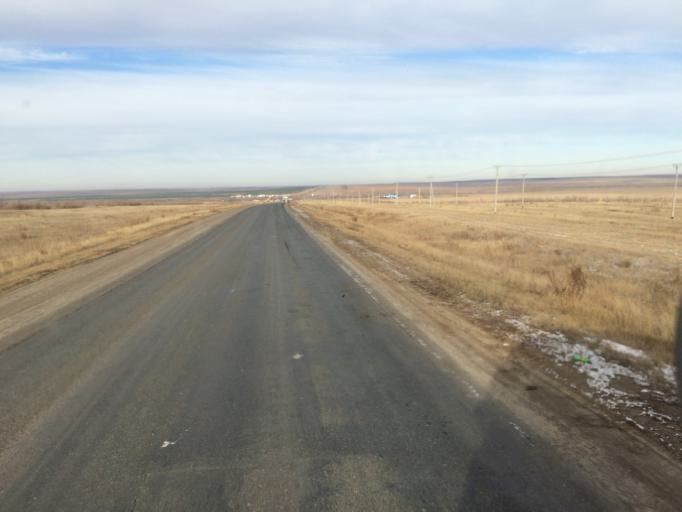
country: KZ
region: Batys Qazaqstan
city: Peremetnoe
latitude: 51.6524
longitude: 51.0106
